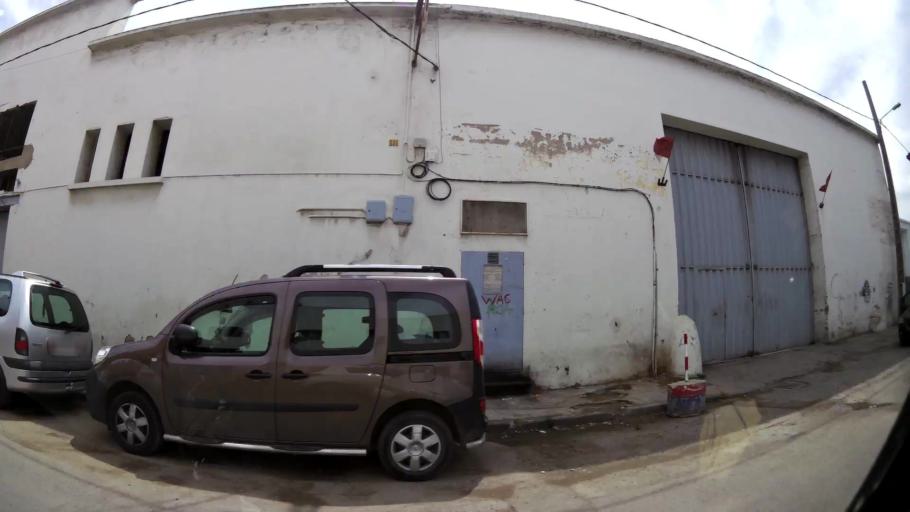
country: MA
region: Grand Casablanca
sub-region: Casablanca
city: Casablanca
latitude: 33.5873
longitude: -7.5749
